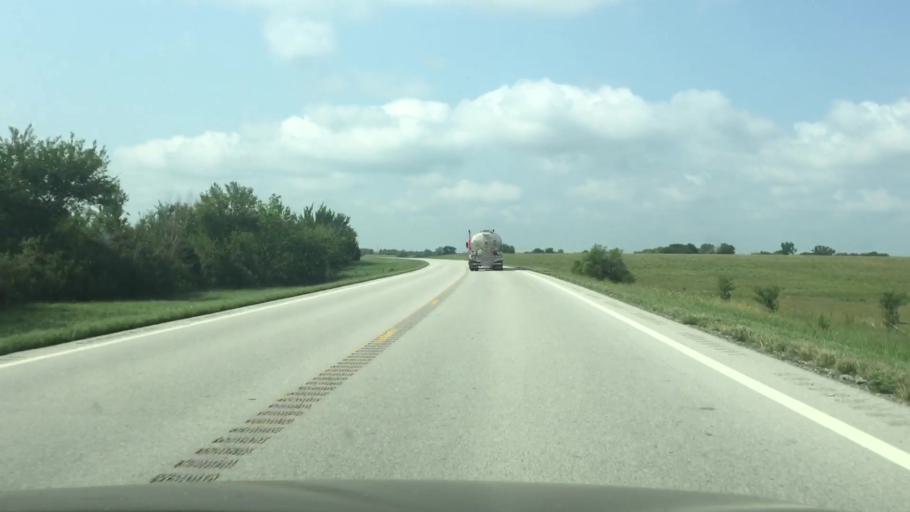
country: US
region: Kansas
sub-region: Anderson County
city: Garnett
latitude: 38.1453
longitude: -95.3258
